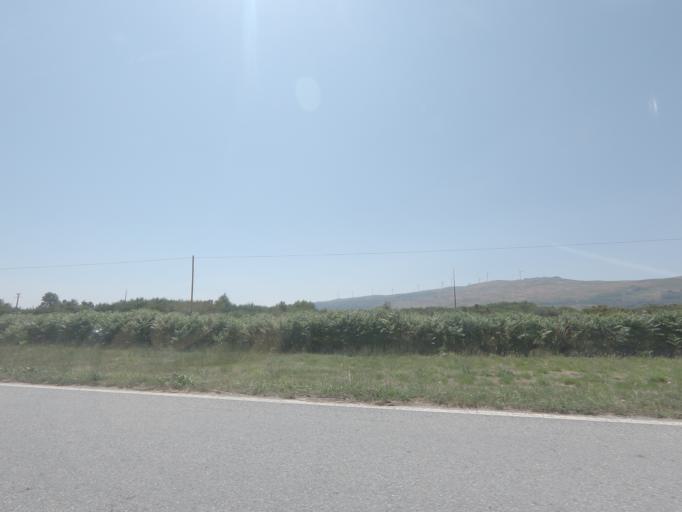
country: PT
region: Viseu
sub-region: Castro Daire
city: Castro Daire
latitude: 40.9679
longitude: -7.8840
